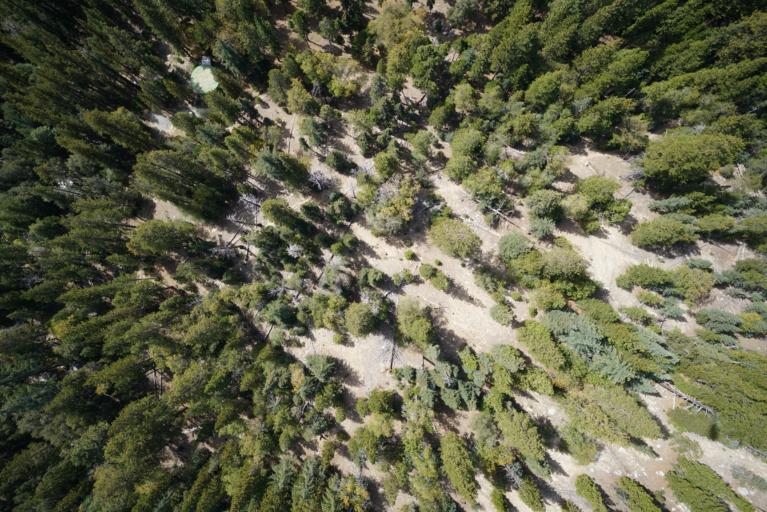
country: US
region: California
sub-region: Riverside County
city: Idyllwild
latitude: 33.7703
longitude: -116.6891
